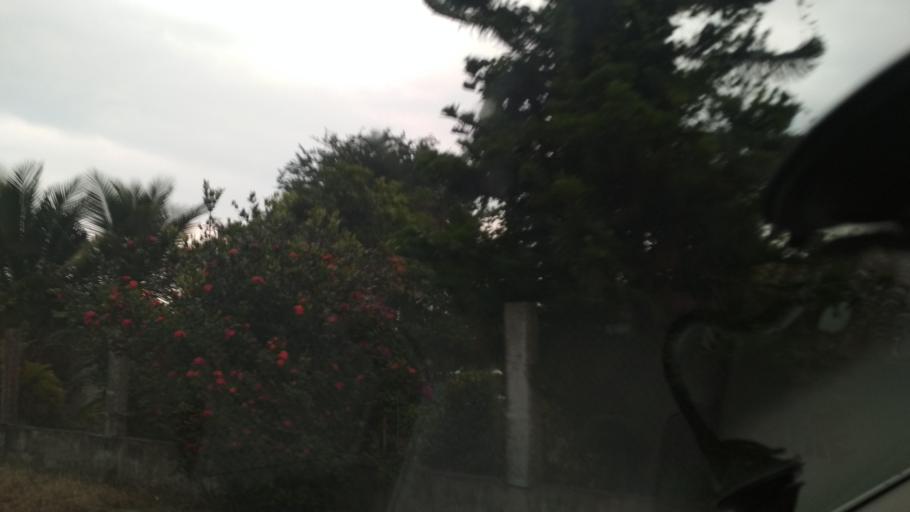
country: MM
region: Shan
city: Taunggyi
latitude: 20.3331
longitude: 97.3105
